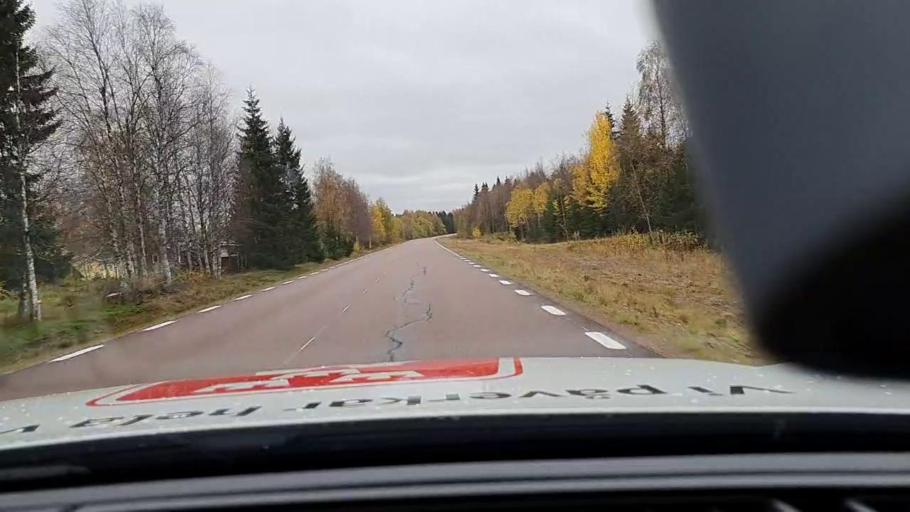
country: FI
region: Lapland
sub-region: Kemi-Tornio
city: Tornio
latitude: 66.0526
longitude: 23.9390
